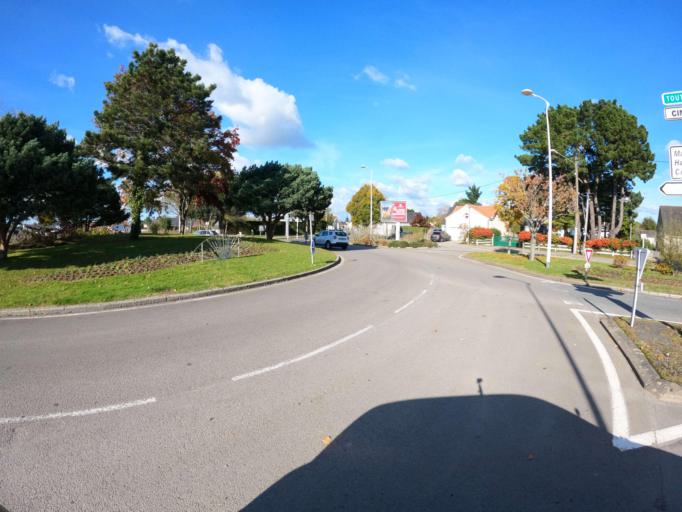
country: FR
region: Pays de la Loire
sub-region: Departement de la Loire-Atlantique
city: La Baule-Escoublac
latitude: 47.2912
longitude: -2.3560
